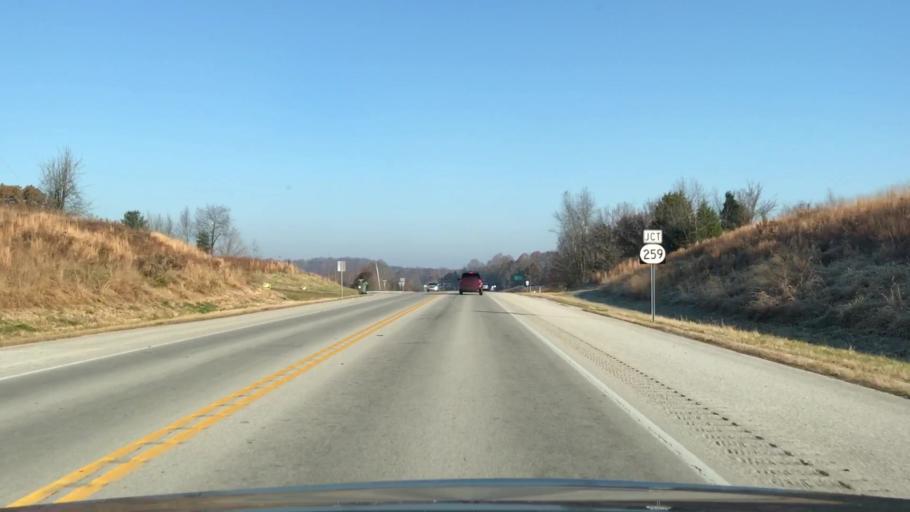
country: US
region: Kentucky
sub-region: Edmonson County
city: Brownsville
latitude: 37.1540
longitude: -86.2214
